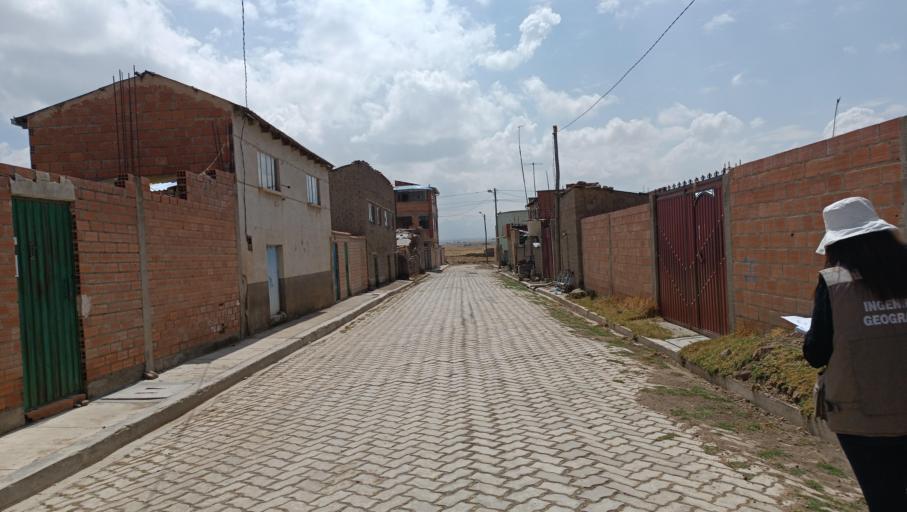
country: BO
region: La Paz
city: Batallas
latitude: -16.3978
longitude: -68.4783
